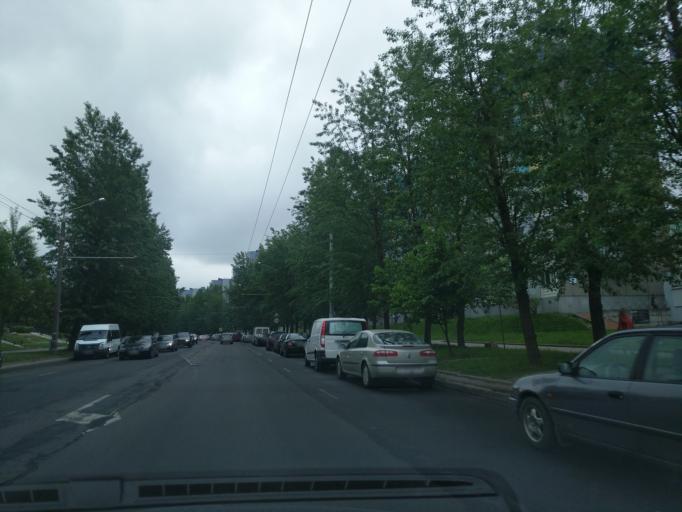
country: BY
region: Minsk
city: Novoye Medvezhino
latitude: 53.8986
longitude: 27.4560
